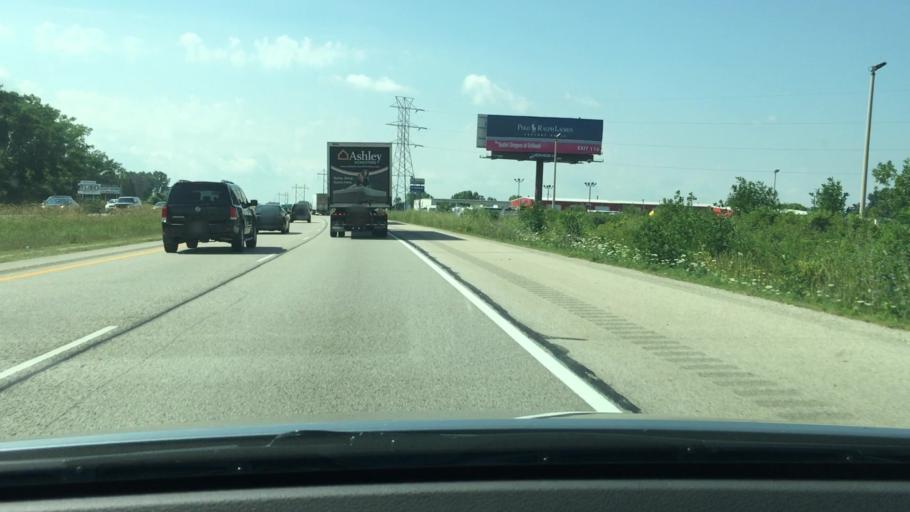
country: US
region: Wisconsin
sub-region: Fond du Lac County
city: North Fond du Lac
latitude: 43.7994
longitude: -88.4883
